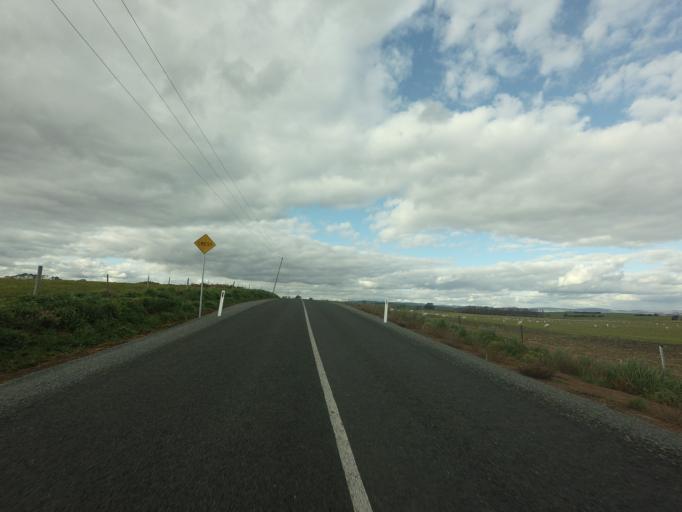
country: AU
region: Tasmania
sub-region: Northern Midlands
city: Evandale
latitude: -41.9114
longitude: 147.3795
